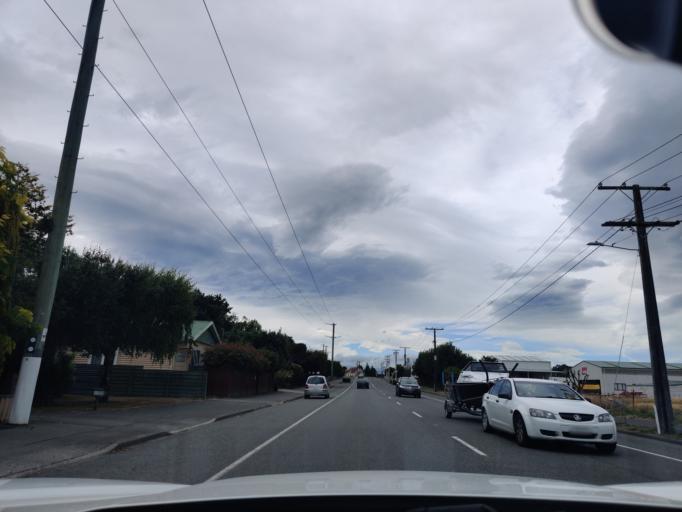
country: NZ
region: Wellington
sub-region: Masterton District
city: Masterton
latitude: -40.9614
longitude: 175.6130
